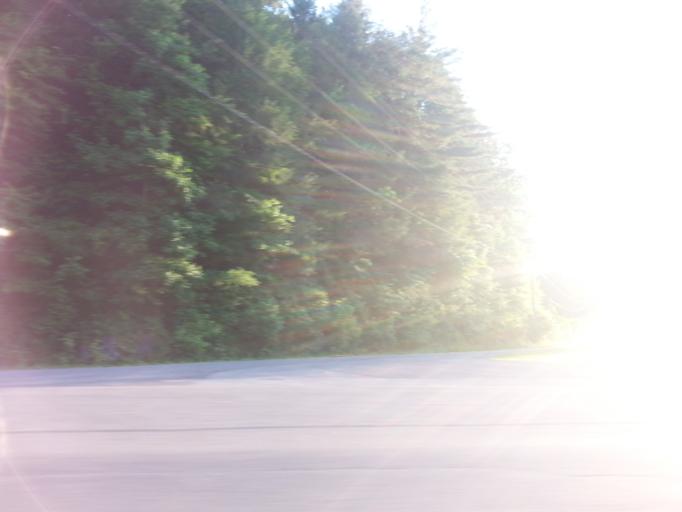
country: US
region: Georgia
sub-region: Fannin County
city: McCaysville
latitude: 35.1504
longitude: -84.3151
